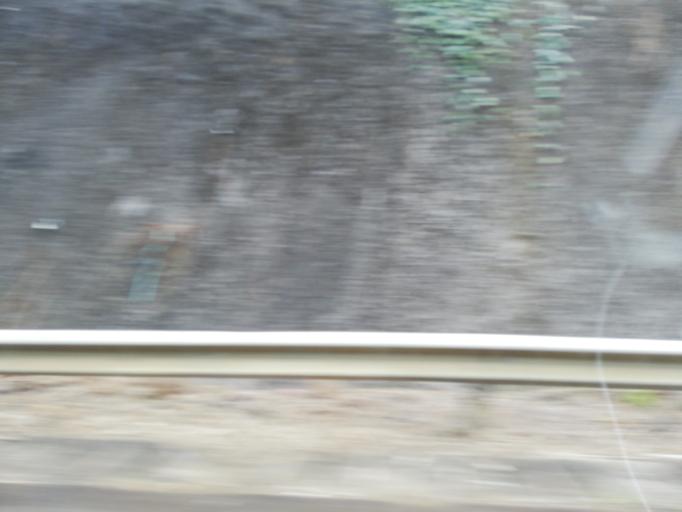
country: MU
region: Grand Port
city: Mahebourg
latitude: -20.3902
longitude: 57.6914
